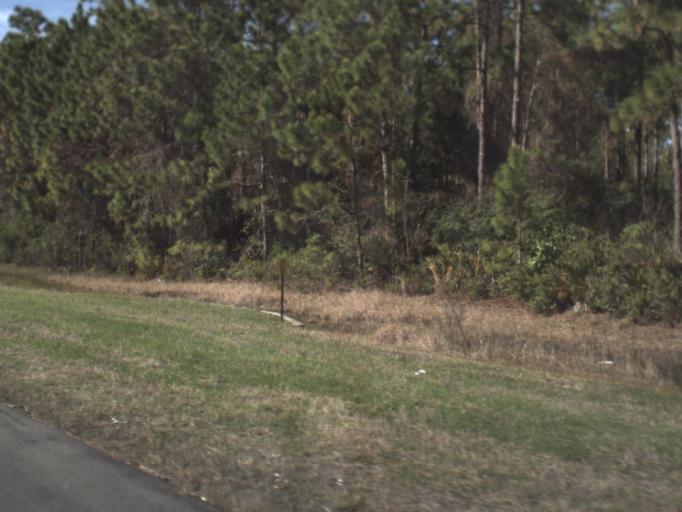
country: US
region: Florida
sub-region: Bay County
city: Panama City Beach
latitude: 30.1936
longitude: -85.8031
